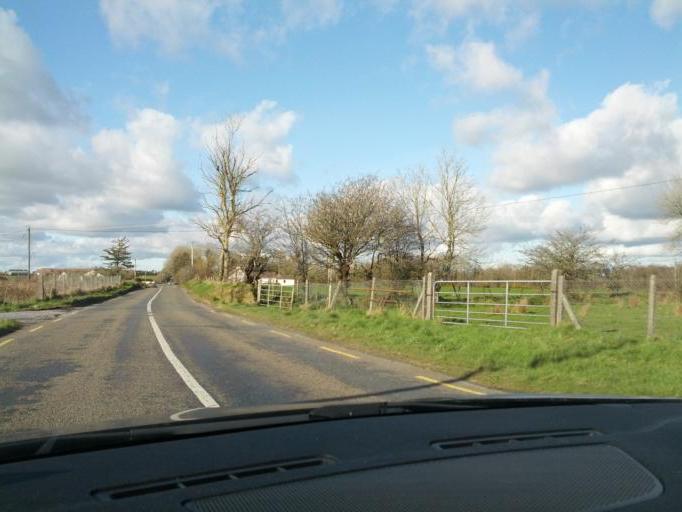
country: IE
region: Connaught
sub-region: Roscommon
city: Castlerea
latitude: 53.5884
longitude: -8.5671
